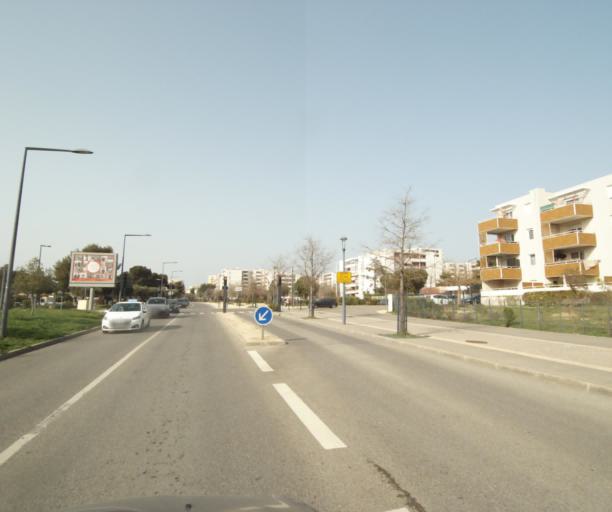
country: FR
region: Provence-Alpes-Cote d'Azur
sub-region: Departement des Bouches-du-Rhone
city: Vitrolles
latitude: 43.4437
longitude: 5.2519
